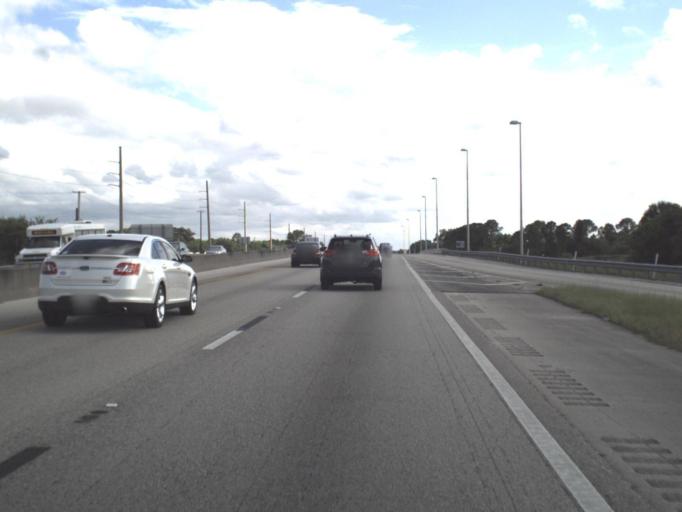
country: US
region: Florida
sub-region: Martin County
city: North River Shores
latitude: 27.2074
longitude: -80.3327
